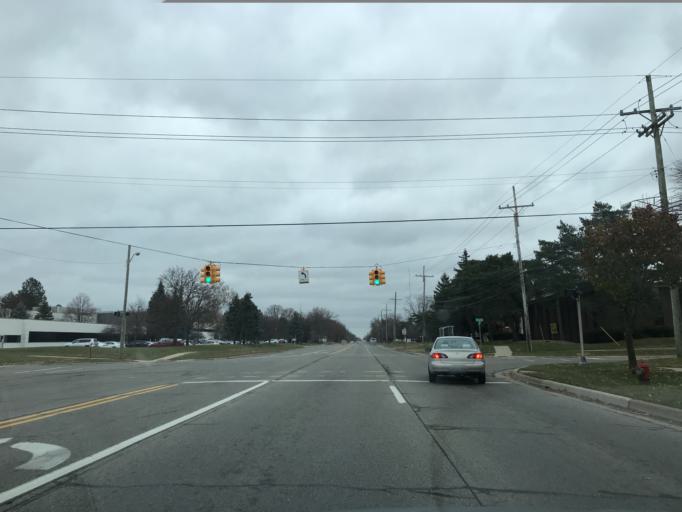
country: US
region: Michigan
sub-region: Oakland County
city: Bingham Farms
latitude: 42.4720
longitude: -83.2795
